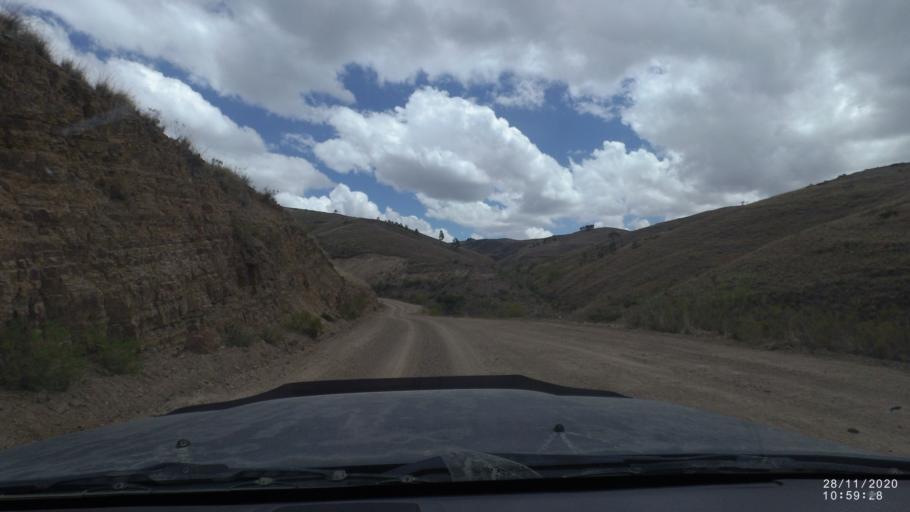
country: BO
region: Cochabamba
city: Capinota
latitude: -17.7730
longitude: -66.1081
